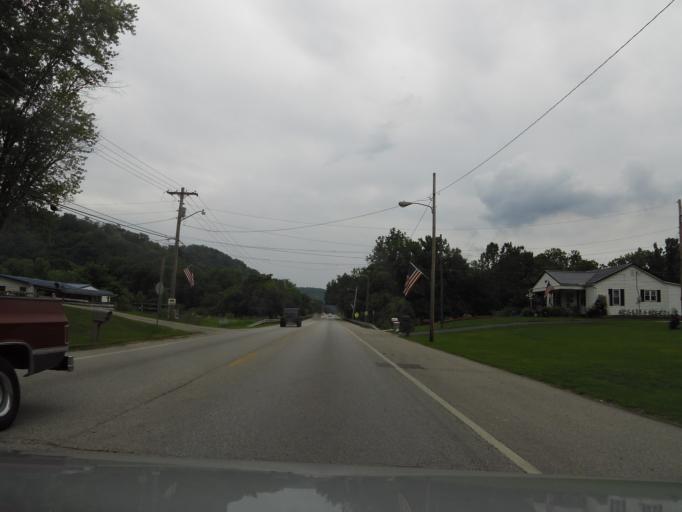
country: US
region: Ohio
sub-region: Brown County
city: Ripley
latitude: 38.7282
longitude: -83.8339
